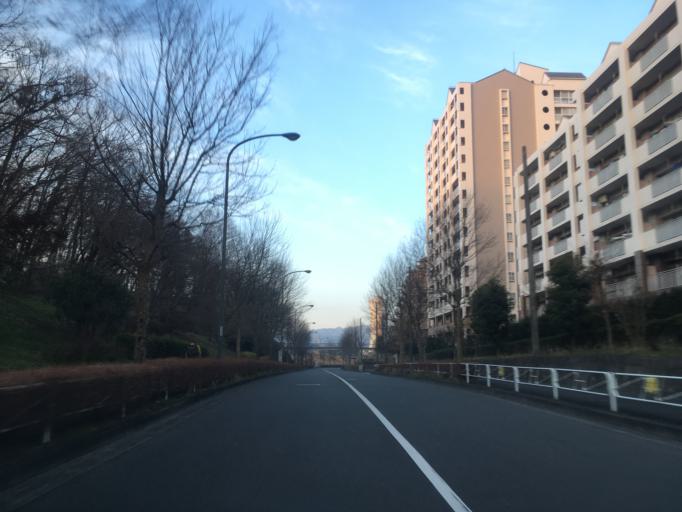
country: JP
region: Tokyo
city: Hachioji
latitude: 35.6086
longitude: 139.3640
